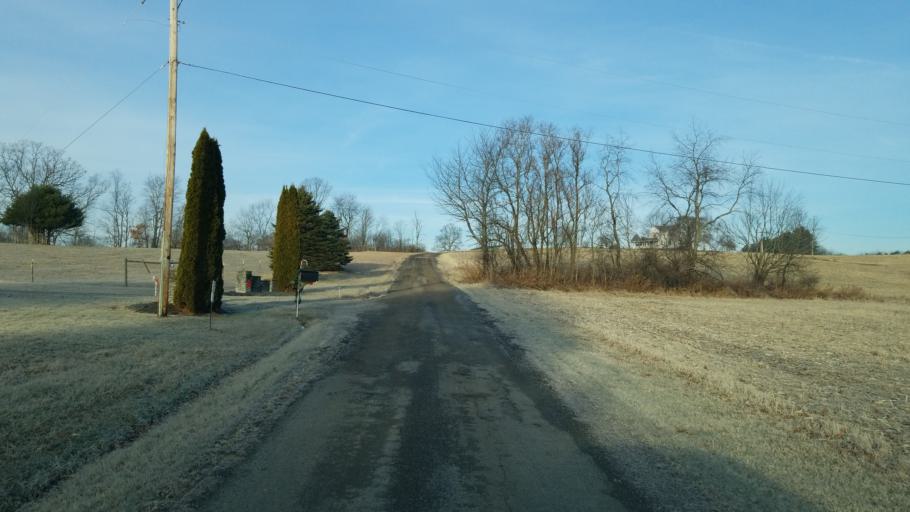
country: US
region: Pennsylvania
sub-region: Indiana County
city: Chevy Chase Heights
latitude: 40.8468
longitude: -79.2603
